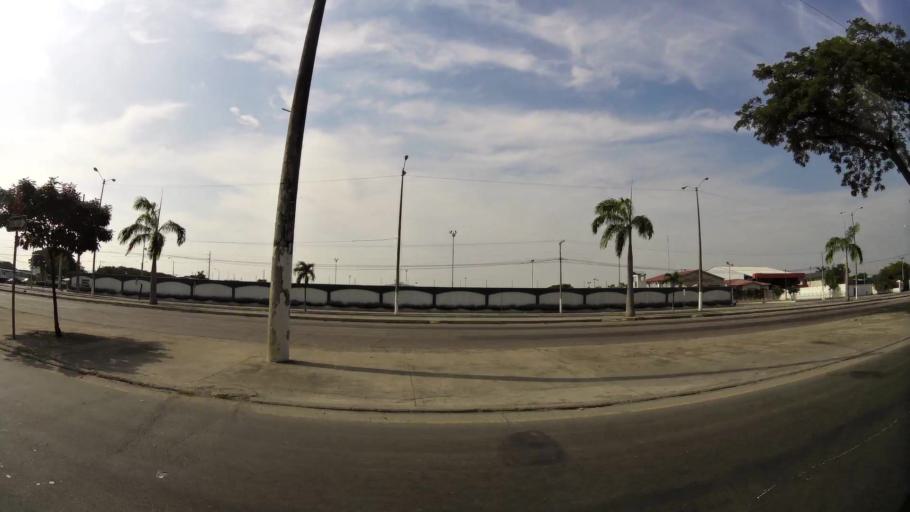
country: EC
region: Guayas
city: Guayaquil
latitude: -2.2715
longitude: -79.9035
